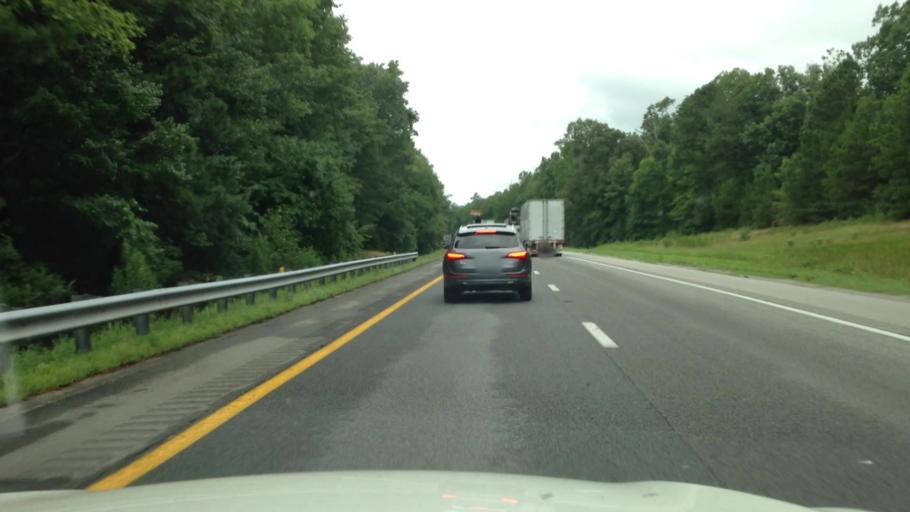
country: US
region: Virginia
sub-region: City of Emporia
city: Emporia
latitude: 36.7551
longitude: -77.5072
